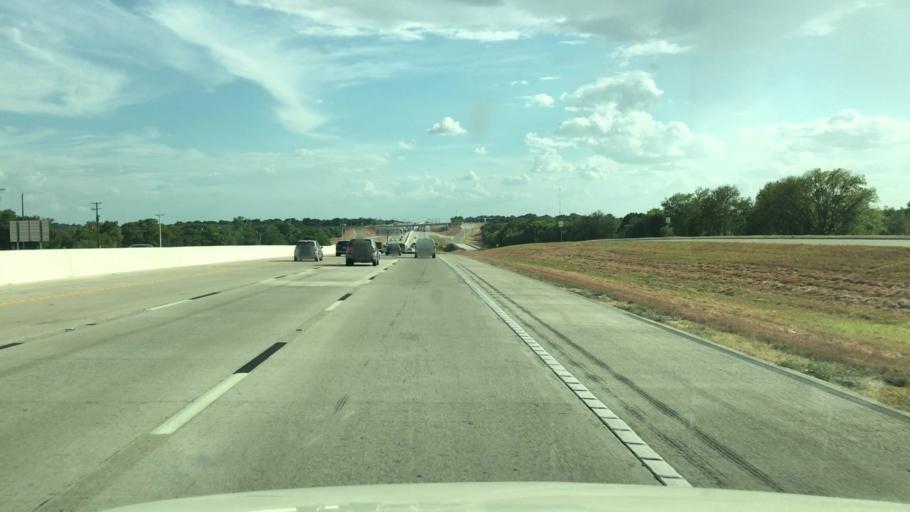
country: US
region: Texas
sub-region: Bell County
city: Belton
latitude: 31.0064
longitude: -97.4891
